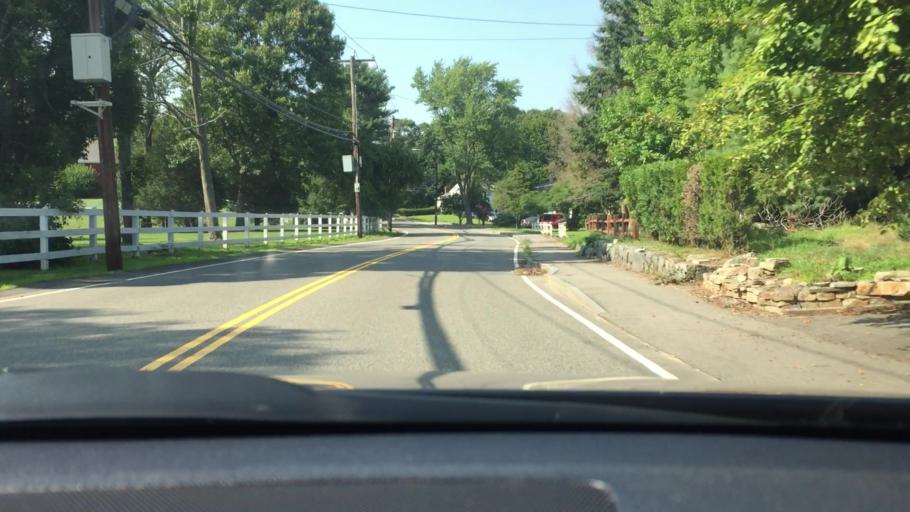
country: US
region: Massachusetts
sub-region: Norfolk County
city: Dedham
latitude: 42.2642
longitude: -71.1835
